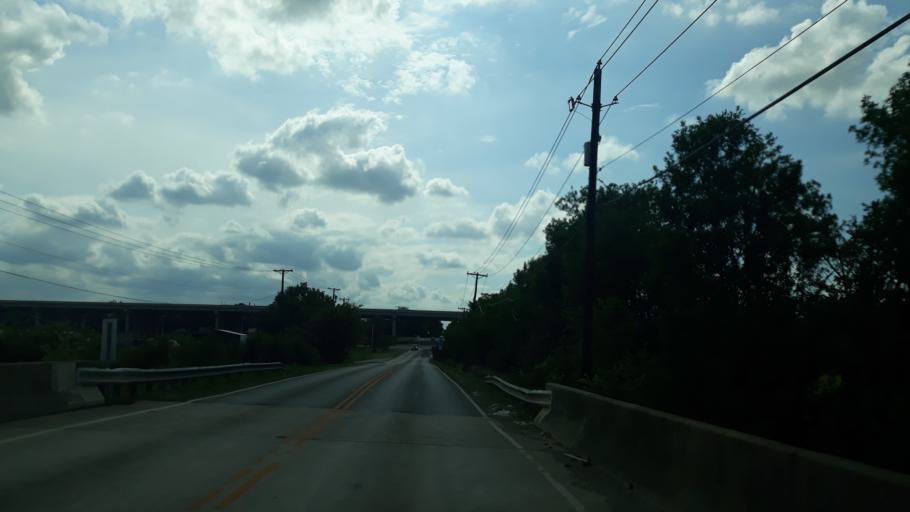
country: US
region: Texas
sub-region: Dallas County
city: Irving
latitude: 32.8158
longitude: -97.0145
